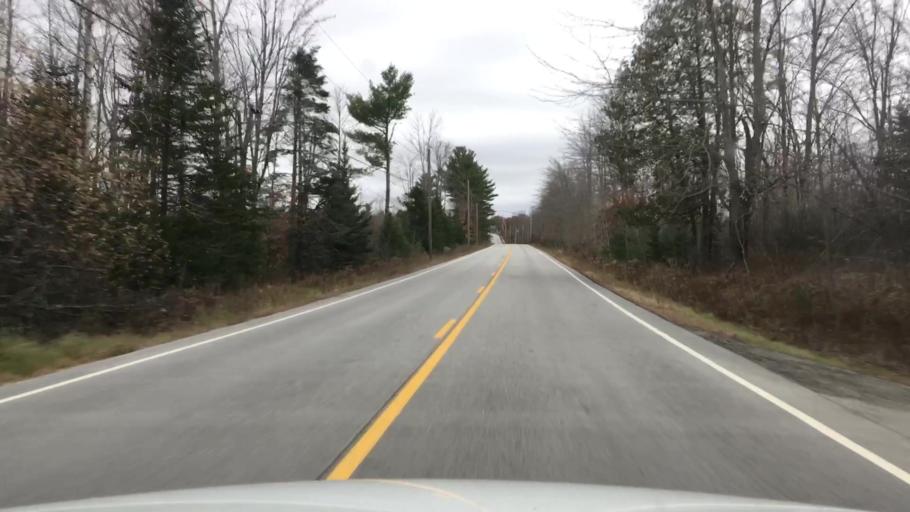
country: US
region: Maine
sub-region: Hancock County
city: Penobscot
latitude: 44.5131
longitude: -68.6575
